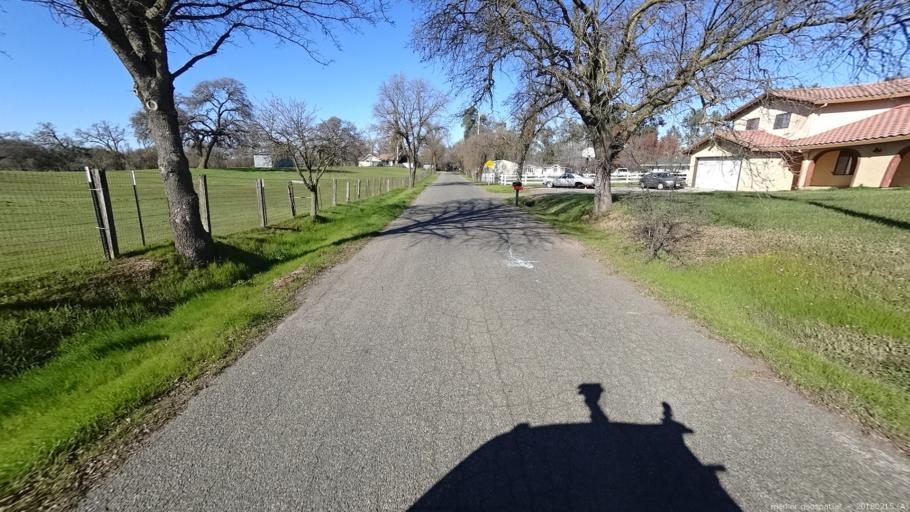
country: US
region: California
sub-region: Sacramento County
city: Rio Linda
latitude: 38.7004
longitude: -121.4152
